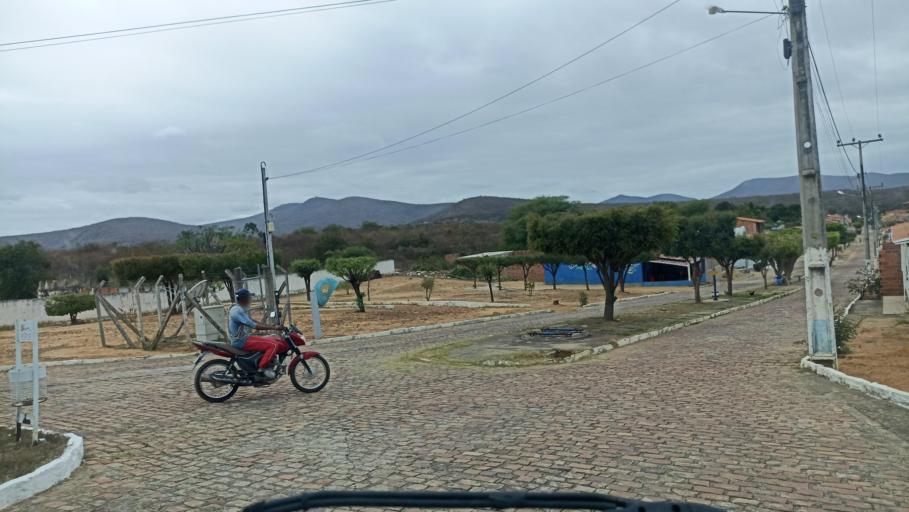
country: BR
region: Bahia
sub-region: Andarai
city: Vera Cruz
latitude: -13.0345
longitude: -40.8180
